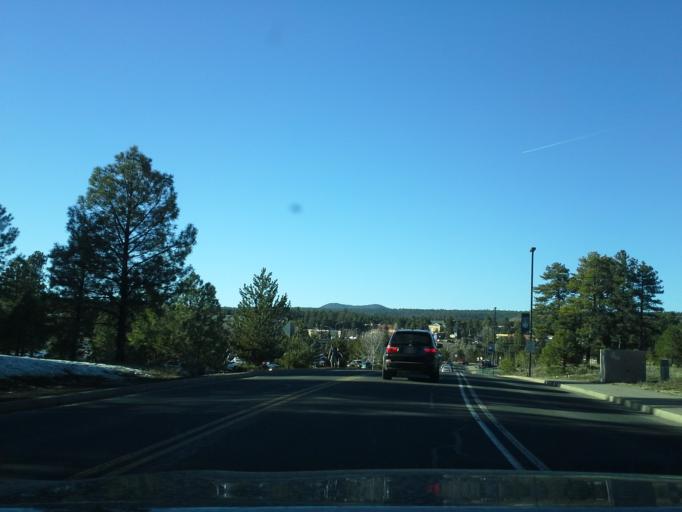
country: US
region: Arizona
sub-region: Coconino County
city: Flagstaff
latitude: 35.1755
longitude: -111.6581
